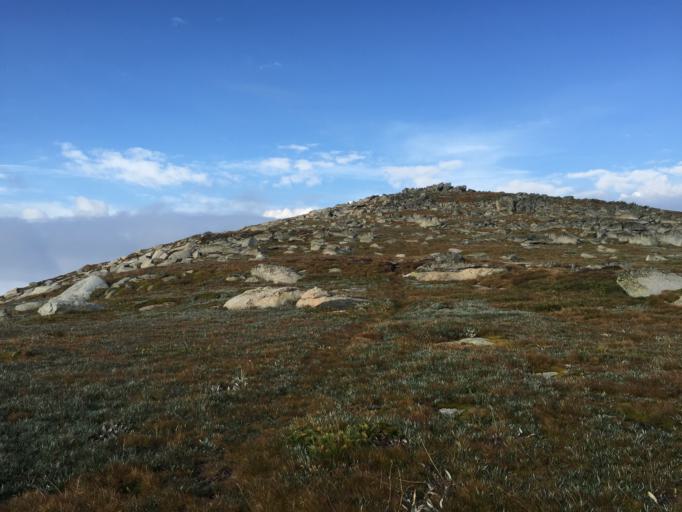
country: AU
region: New South Wales
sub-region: Snowy River
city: Jindabyne
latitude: -36.4546
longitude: 148.2639
